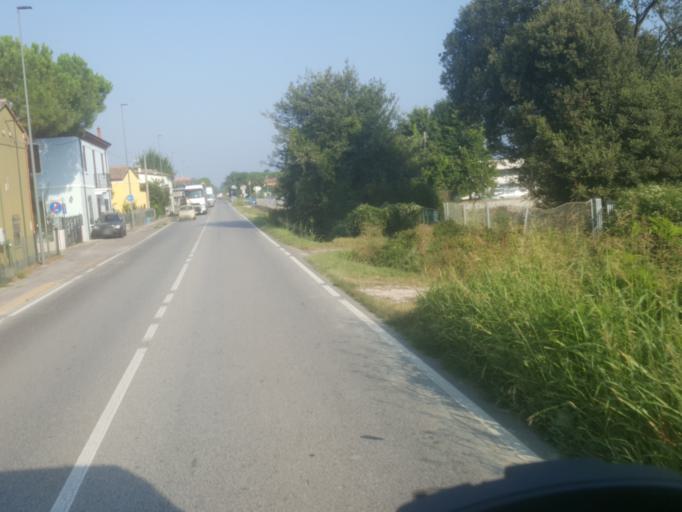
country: IT
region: Emilia-Romagna
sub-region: Provincia di Ravenna
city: Mezzano
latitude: 44.4580
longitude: 12.1020
